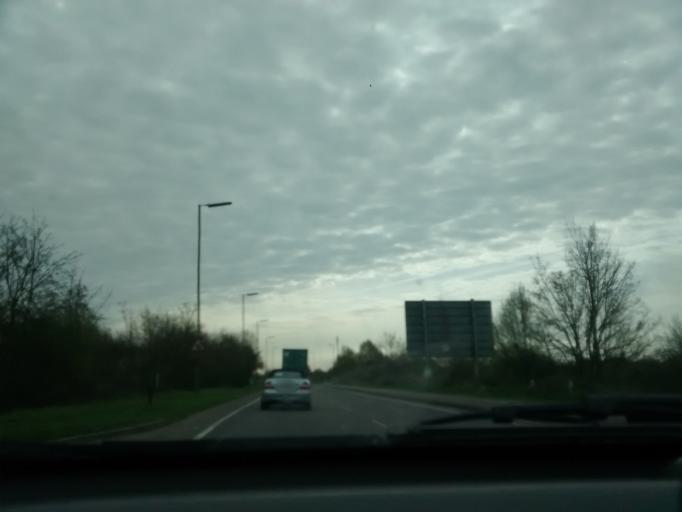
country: GB
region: England
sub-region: Oxfordshire
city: Bicester
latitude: 51.9138
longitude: -1.1424
